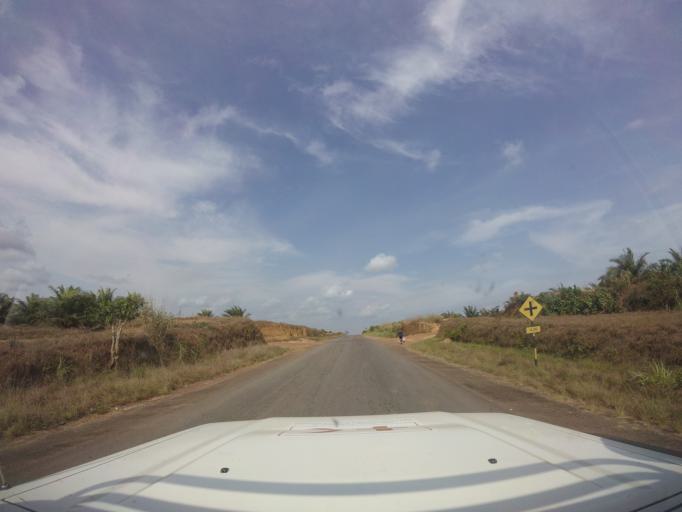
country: LR
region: Bomi
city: Tubmanburg
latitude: 6.7280
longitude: -11.0320
